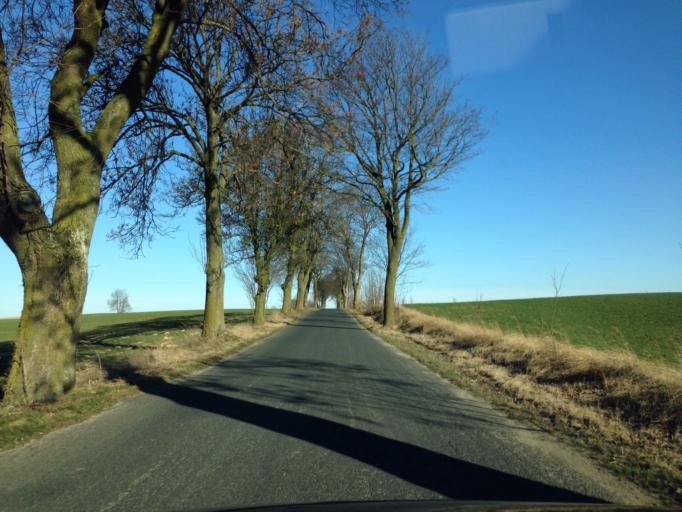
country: PL
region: Kujawsko-Pomorskie
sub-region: Powiat brodnicki
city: Brzozie
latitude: 53.3607
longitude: 19.6330
